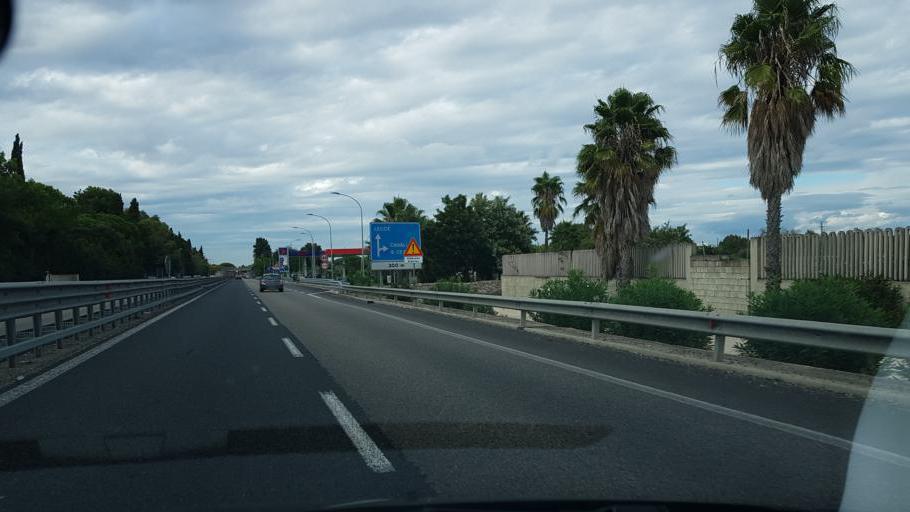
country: IT
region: Apulia
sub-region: Provincia di Lecce
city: Cavallino
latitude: 40.3031
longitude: 18.1924
